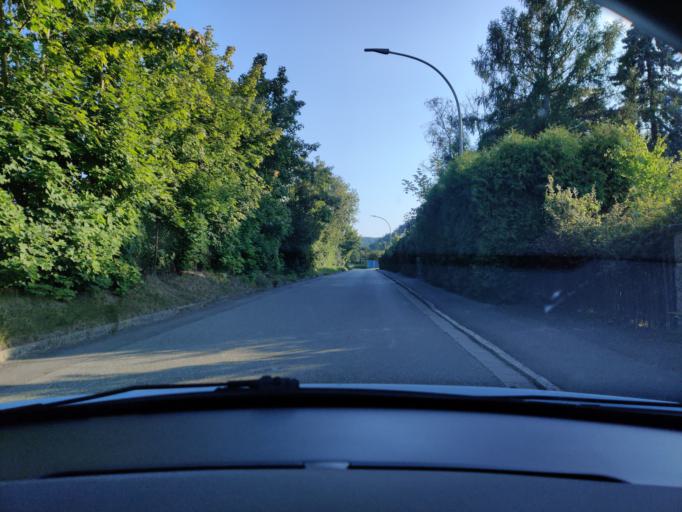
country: DE
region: Bavaria
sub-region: Upper Palatinate
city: Nabburg
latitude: 49.4462
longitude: 12.1783
